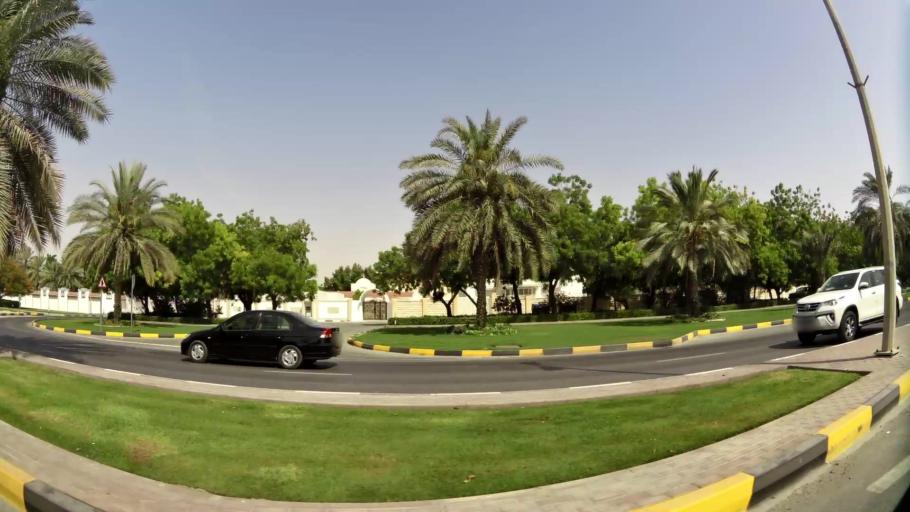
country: AE
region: Ash Shariqah
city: Sharjah
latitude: 25.3329
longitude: 55.4384
